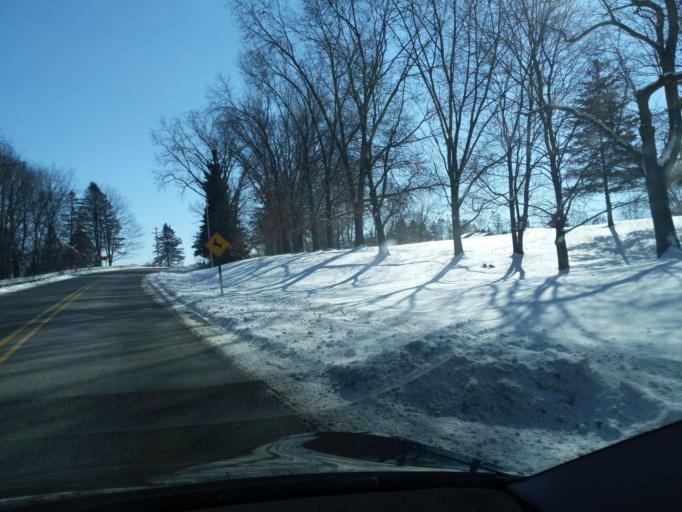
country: US
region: Michigan
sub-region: Ingham County
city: Stockbridge
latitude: 42.4940
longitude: -84.0875
